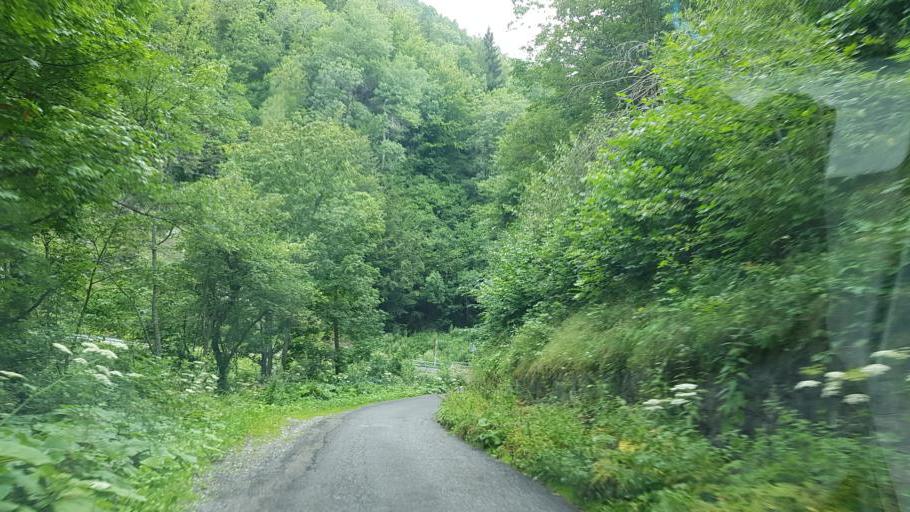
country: IT
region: Piedmont
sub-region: Provincia di Cuneo
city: Stroppo
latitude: 44.5216
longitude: 7.1241
